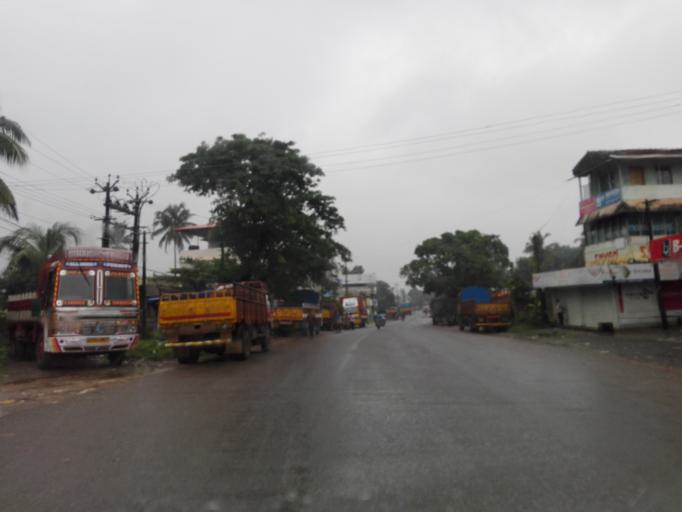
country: IN
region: Kerala
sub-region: Ernakulam
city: Elur
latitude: 10.0642
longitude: 76.3222
